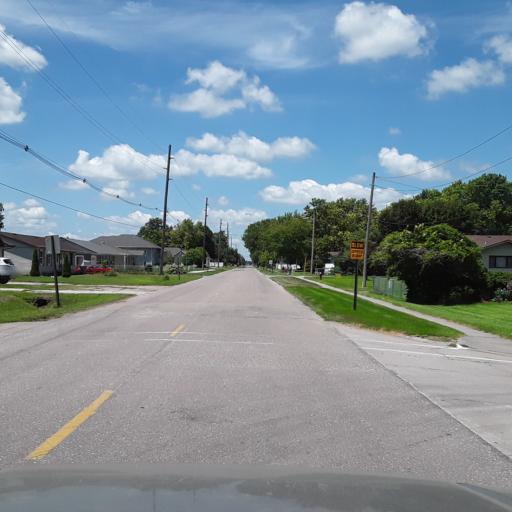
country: US
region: Nebraska
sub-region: Merrick County
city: Central City
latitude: 41.1048
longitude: -98.0038
